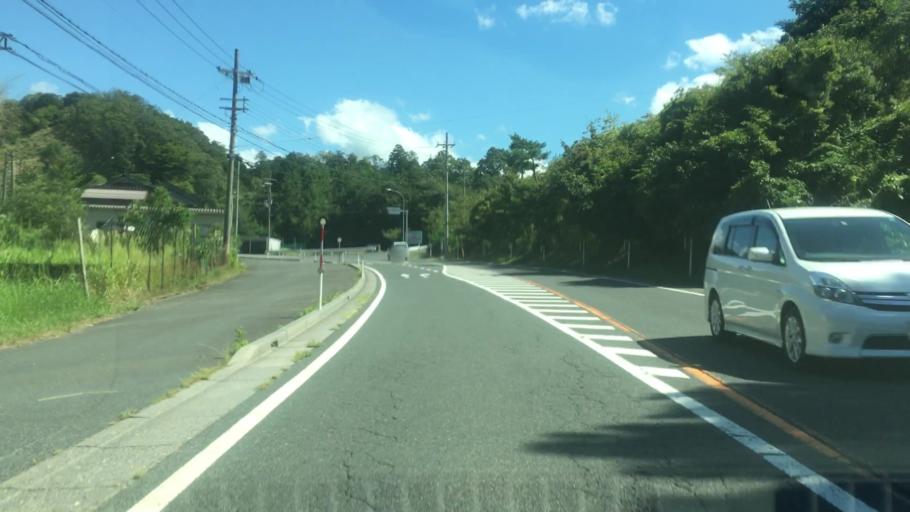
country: JP
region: Hyogo
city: Toyooka
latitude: 35.5846
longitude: 134.9534
